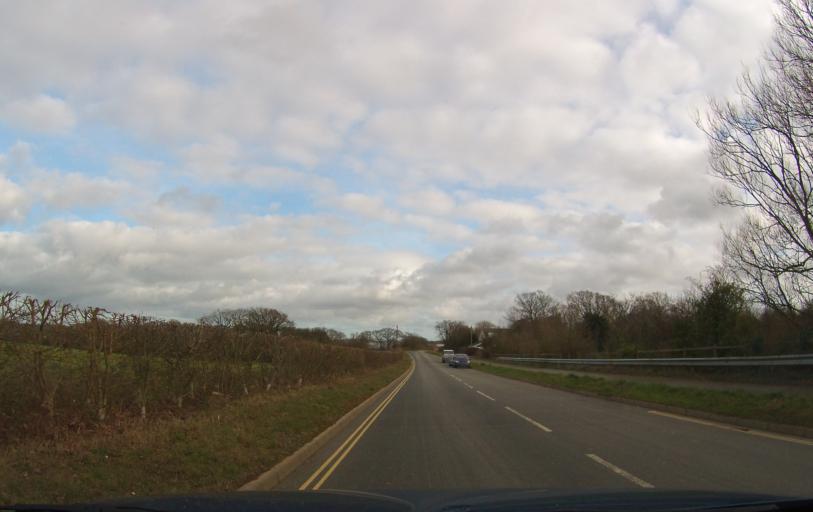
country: GB
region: England
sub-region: Isle of Wight
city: Newport
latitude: 50.7238
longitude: -1.2961
